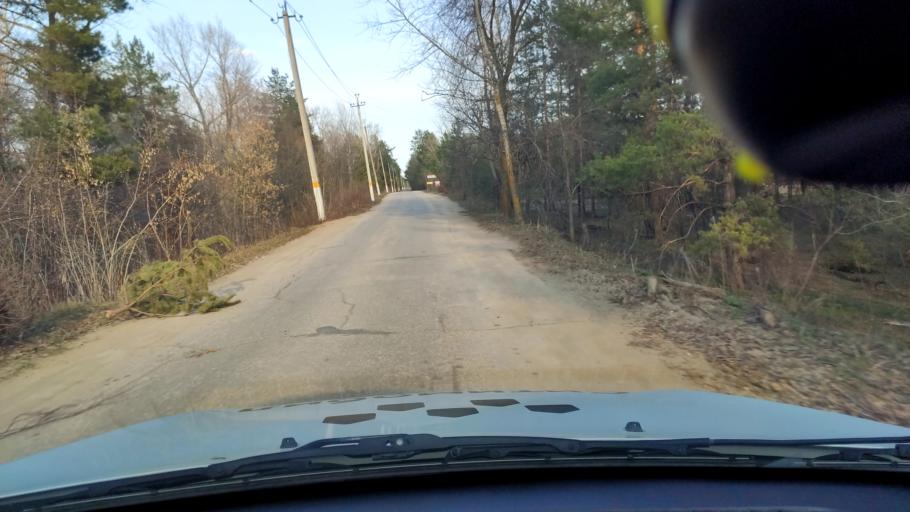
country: RU
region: Samara
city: Zhigulevsk
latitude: 53.4582
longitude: 49.6065
